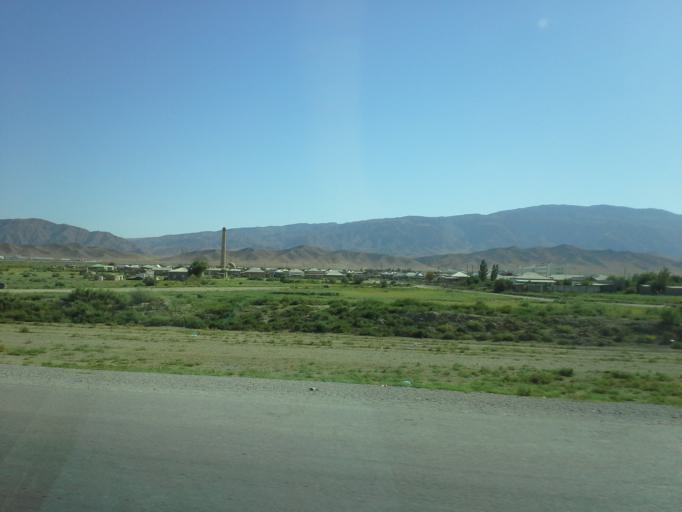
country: TM
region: Ahal
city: Baharly
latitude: 38.3789
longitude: 57.5042
